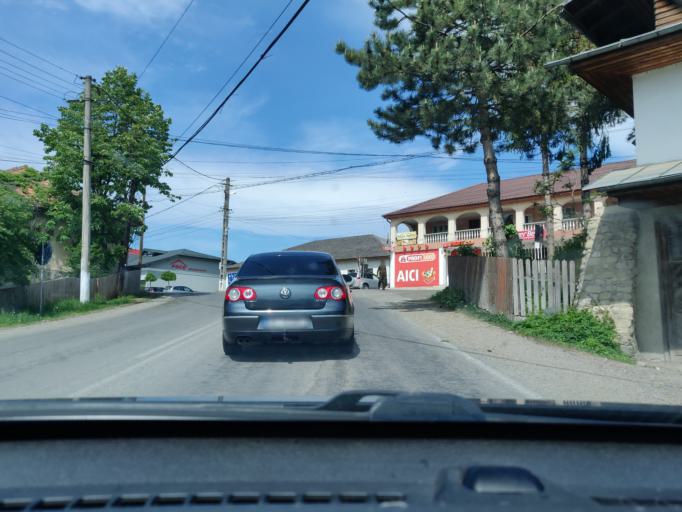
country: RO
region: Vrancea
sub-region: Comuna Vidra
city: Vidra
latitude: 45.9105
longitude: 26.9076
